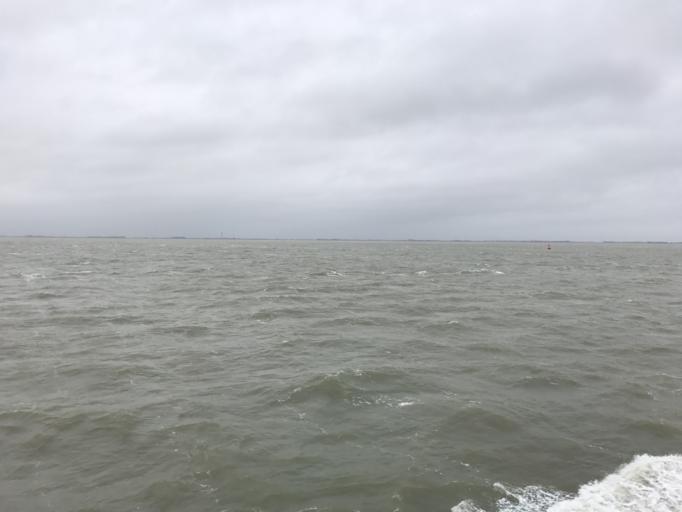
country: NL
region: Groningen
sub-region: Gemeente Delfzijl
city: Delfzijl
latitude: 53.4088
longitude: 6.9428
